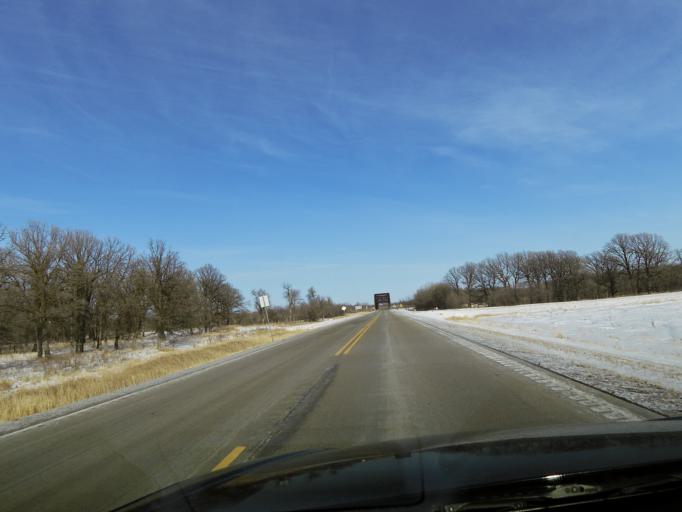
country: US
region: North Dakota
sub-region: Walsh County
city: Grafton
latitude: 48.4118
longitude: -97.1417
